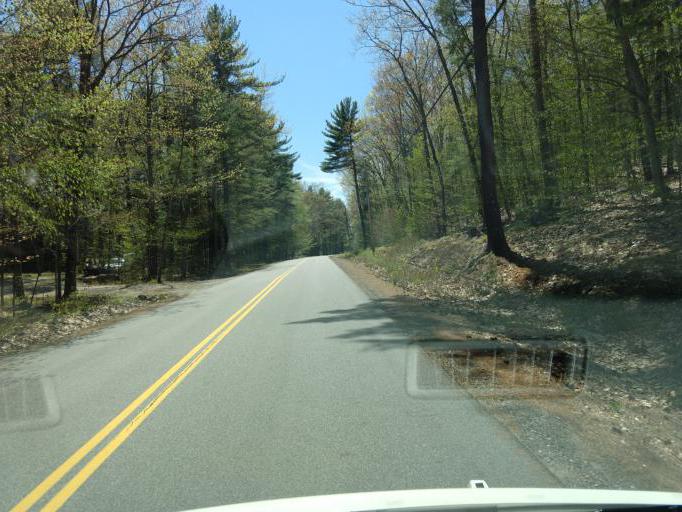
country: US
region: Maine
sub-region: York County
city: Ogunquit
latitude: 43.2315
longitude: -70.6225
